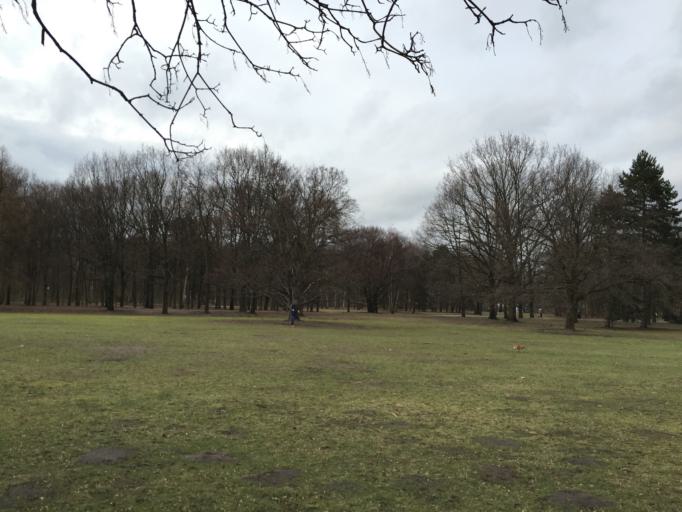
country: DE
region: Berlin
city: Tiergarten Bezirk
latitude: 52.5131
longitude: 13.3747
